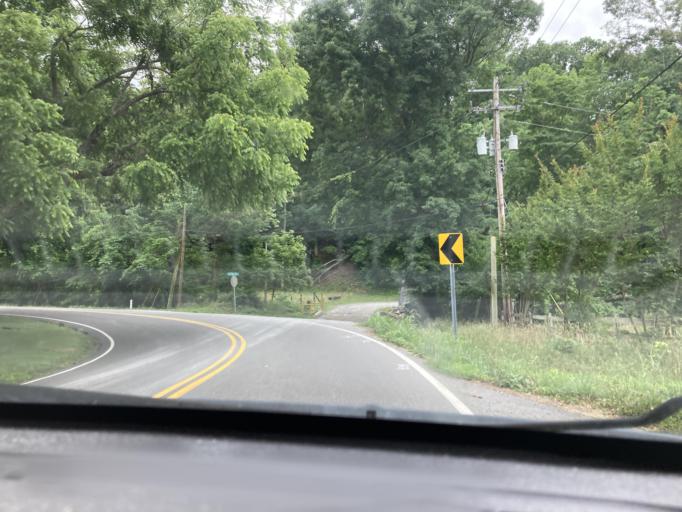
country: US
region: Tennessee
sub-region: Dickson County
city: Dickson
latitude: 36.0415
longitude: -87.3684
